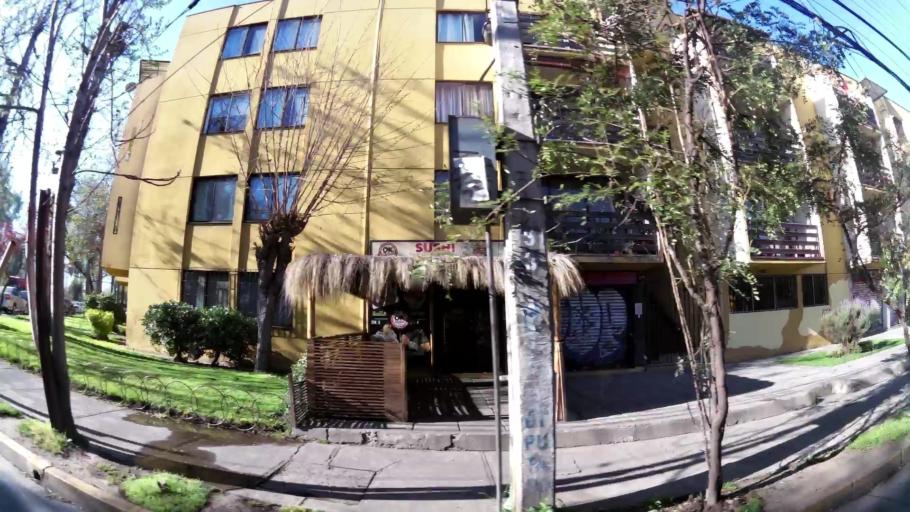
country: CL
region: Santiago Metropolitan
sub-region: Provincia de Santiago
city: Villa Presidente Frei, Nunoa, Santiago, Chile
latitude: -33.4523
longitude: -70.5593
